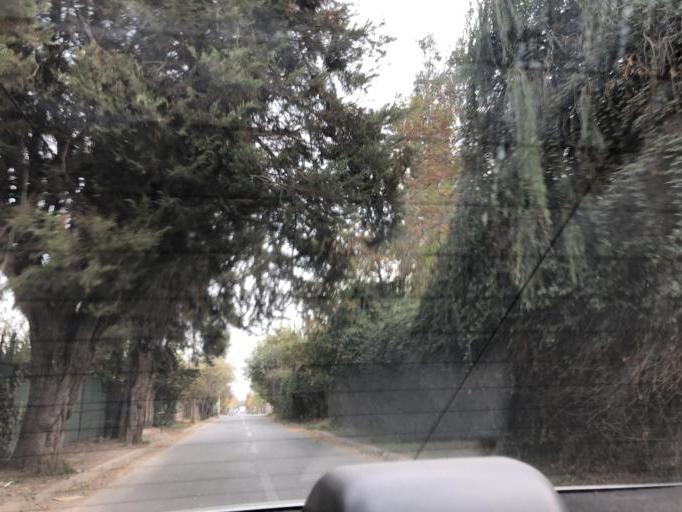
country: CL
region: Santiago Metropolitan
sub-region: Provincia de Cordillera
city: Puente Alto
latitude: -33.6119
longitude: -70.5313
